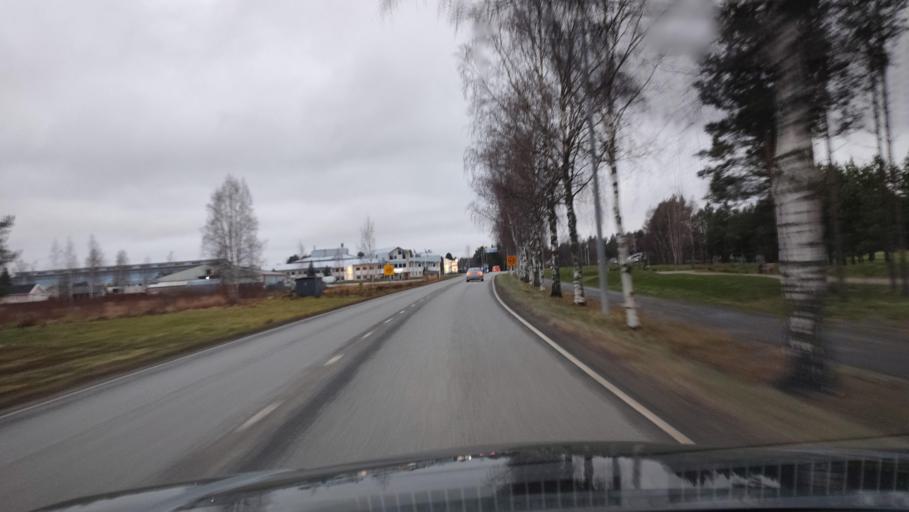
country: FI
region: Southern Ostrobothnia
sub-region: Suupohja
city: Kauhajoki
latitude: 62.4172
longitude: 22.1792
